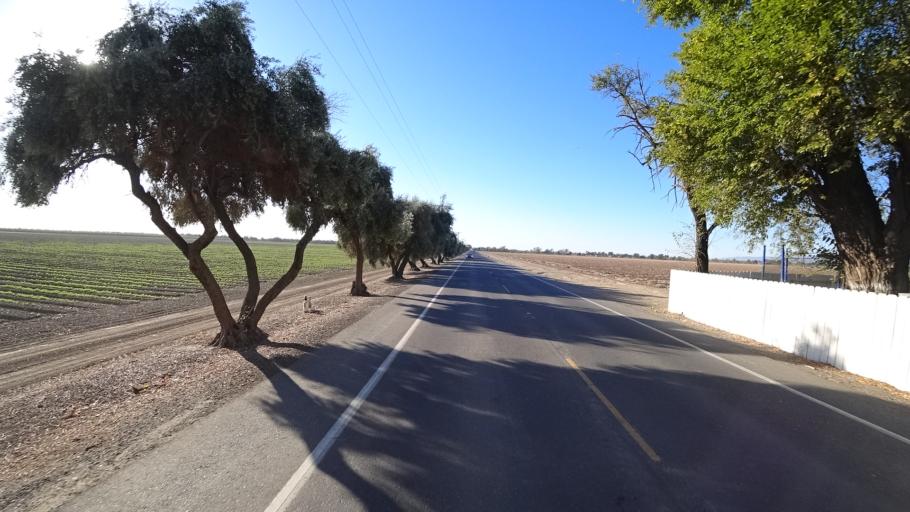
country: US
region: California
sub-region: Yolo County
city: Woodland
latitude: 38.6172
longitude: -121.7851
